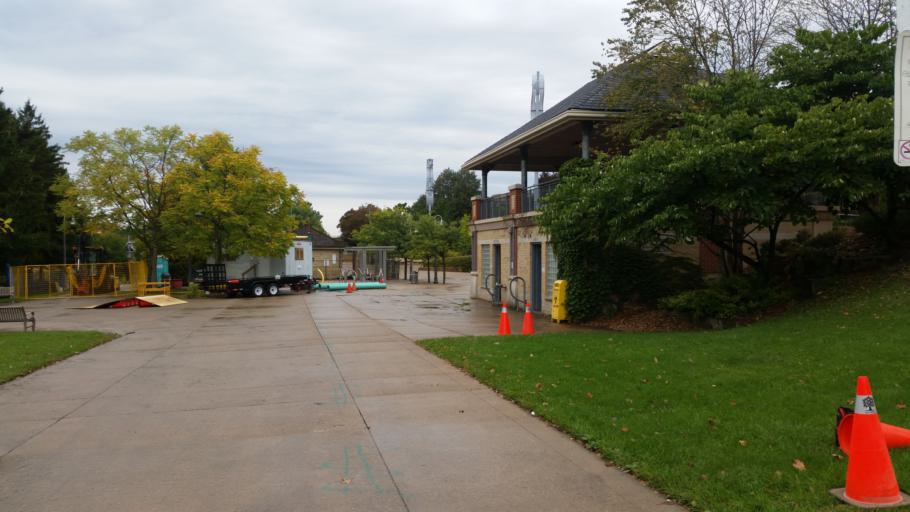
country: CA
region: Ontario
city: London
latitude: 42.9811
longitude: -81.2556
